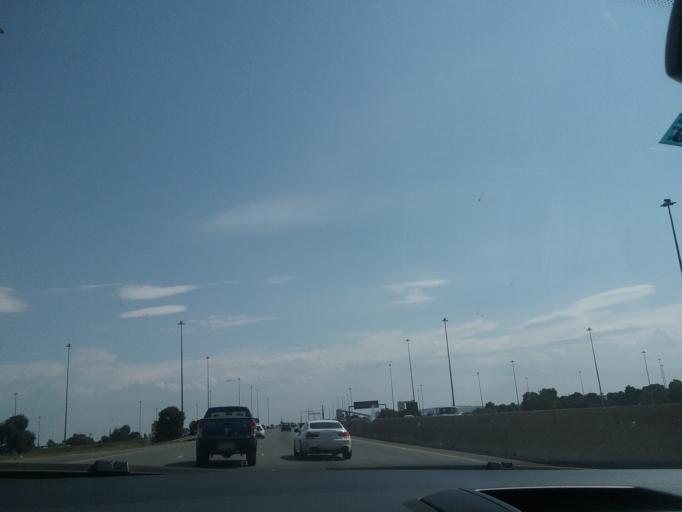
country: ZA
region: Gauteng
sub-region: Ekurhuleni Metropolitan Municipality
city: Germiston
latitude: -26.2097
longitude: 28.1364
